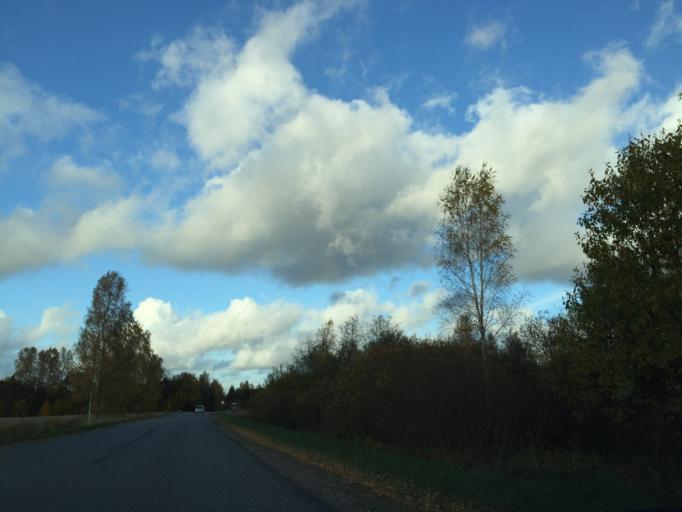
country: LV
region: Ogre
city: Jumprava
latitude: 56.7745
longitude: 25.0040
